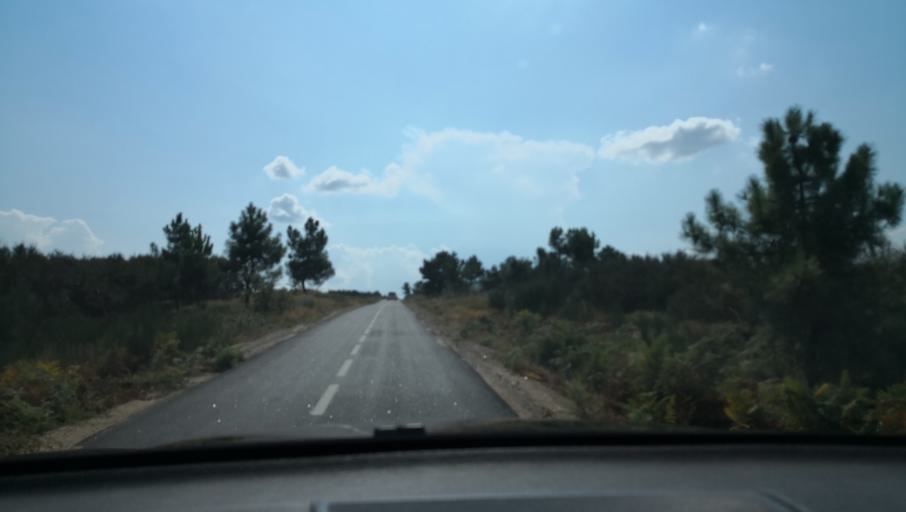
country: PT
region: Vila Real
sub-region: Sabrosa
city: Sabrosa
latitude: 41.2919
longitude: -7.6128
